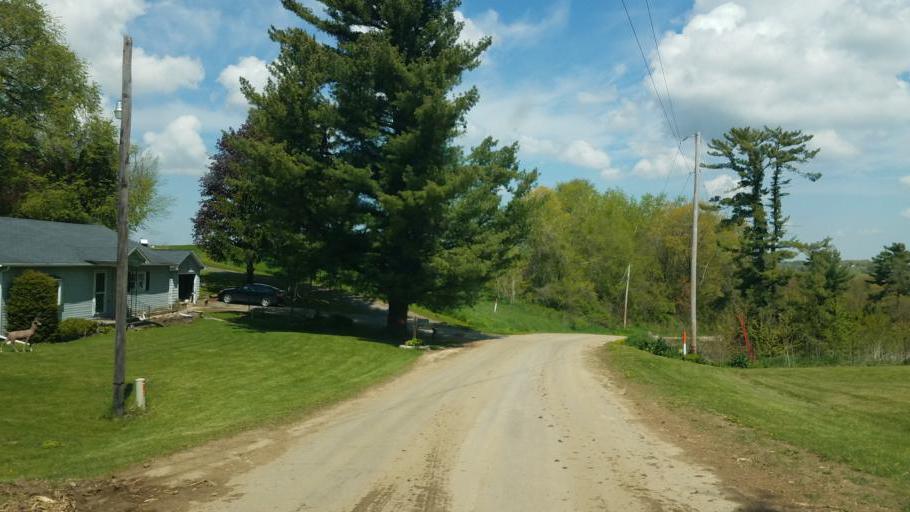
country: US
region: Wisconsin
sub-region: Juneau County
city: Elroy
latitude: 43.6924
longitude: -90.2911
